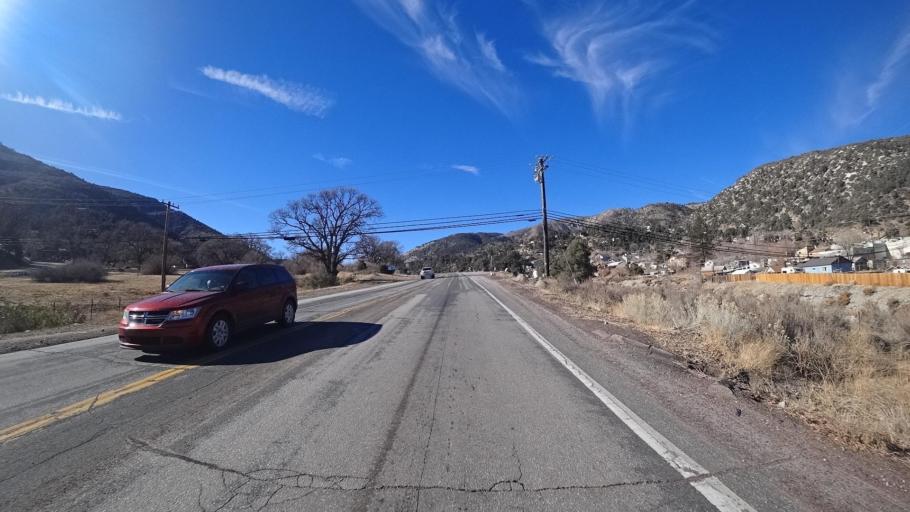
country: US
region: California
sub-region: Kern County
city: Frazier Park
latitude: 34.8213
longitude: -118.9463
